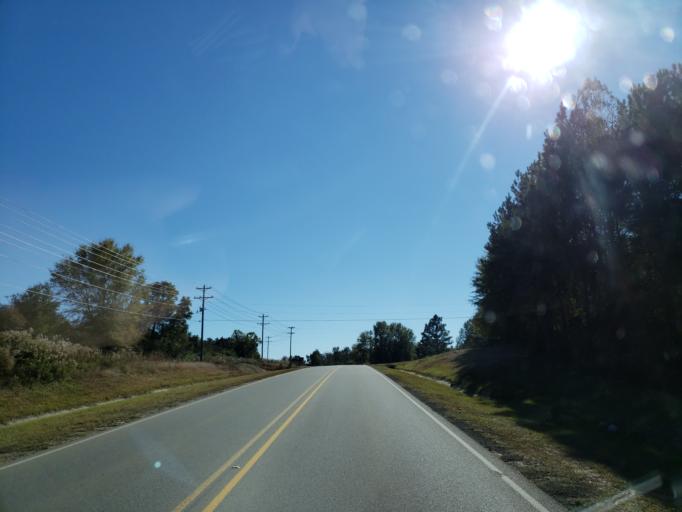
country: US
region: Mississippi
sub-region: Lamar County
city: West Hattiesburg
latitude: 31.3287
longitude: -89.3998
